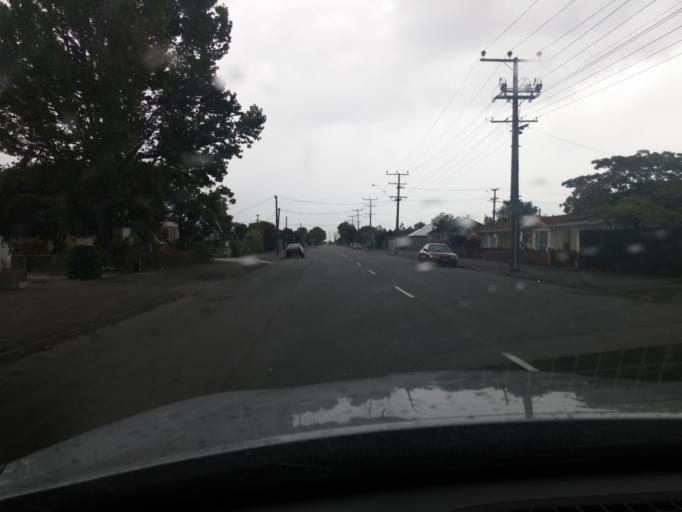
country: NZ
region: Marlborough
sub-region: Marlborough District
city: Blenheim
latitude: -41.5045
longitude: 173.9554
